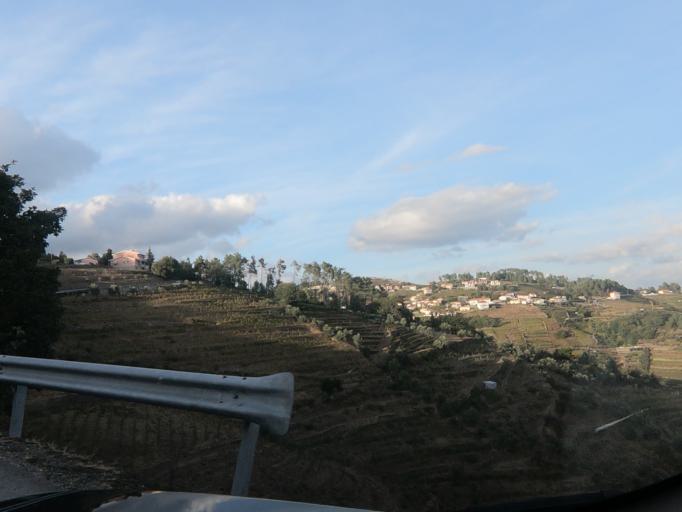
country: PT
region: Vila Real
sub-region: Santa Marta de Penaguiao
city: Santa Marta de Penaguiao
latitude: 41.2200
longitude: -7.8165
